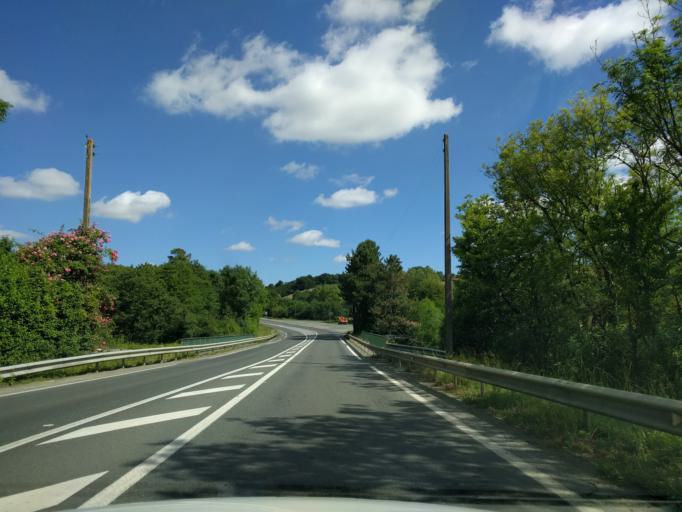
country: FR
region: Pays de la Loire
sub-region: Departement de la Vendee
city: Chantonnay
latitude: 46.6590
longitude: -1.0443
